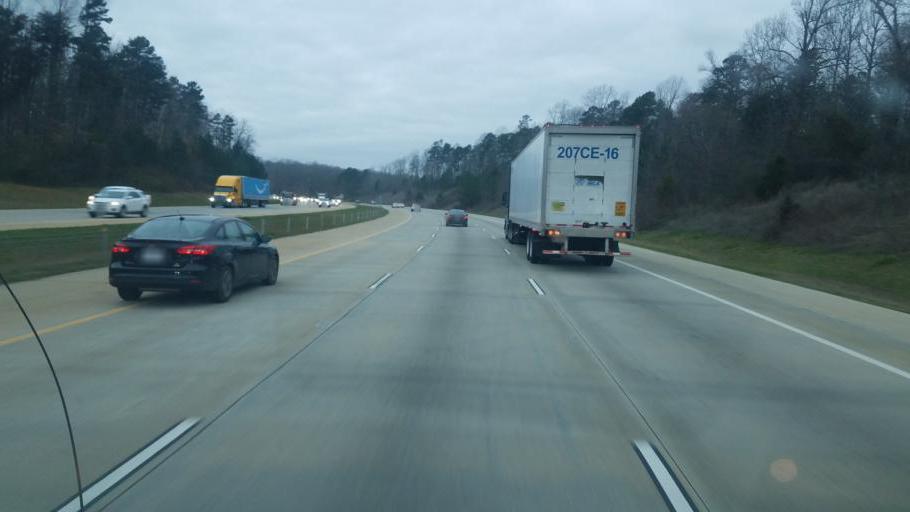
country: US
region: North Carolina
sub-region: Mecklenburg County
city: Huntersville
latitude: 35.3403
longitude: -80.8997
